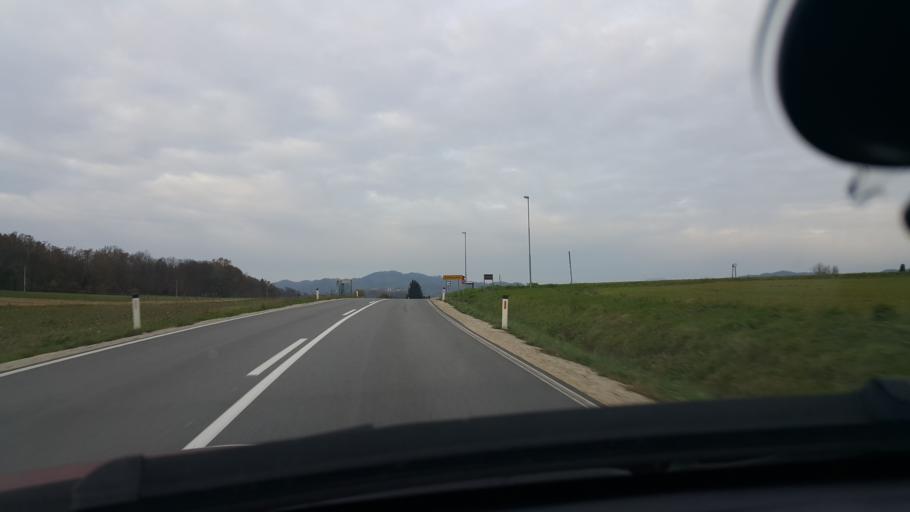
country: SI
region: Kozje
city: Kozje
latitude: 46.0990
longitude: 15.6118
